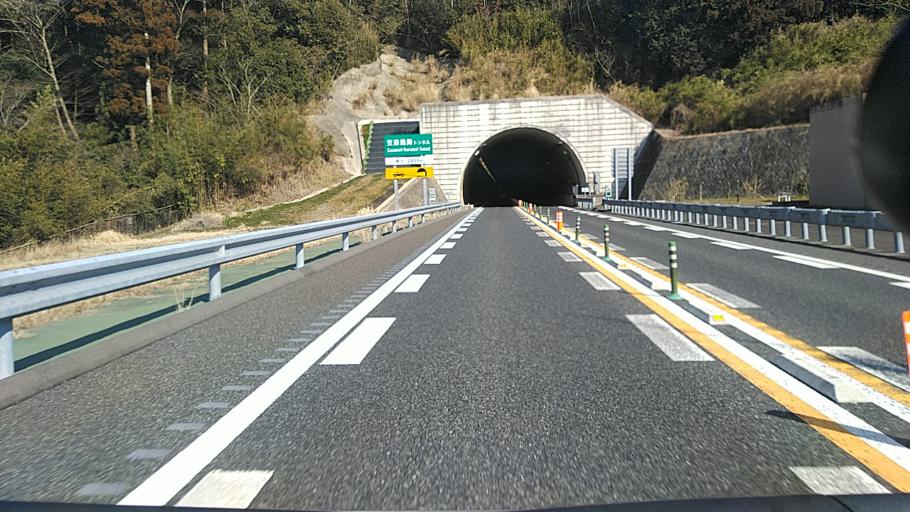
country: JP
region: Chiba
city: Mobara
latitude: 35.3621
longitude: 140.1879
